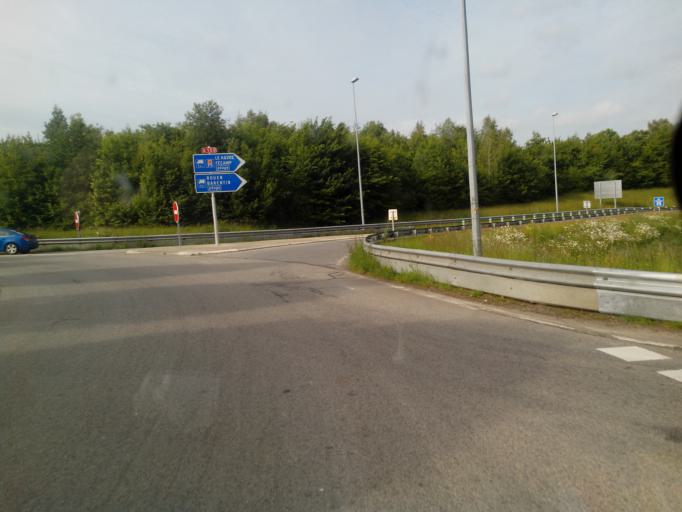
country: FR
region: Haute-Normandie
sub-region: Departement de la Seine-Maritime
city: Sainte-Marie-des-Champs
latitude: 49.6277
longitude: 0.8020
